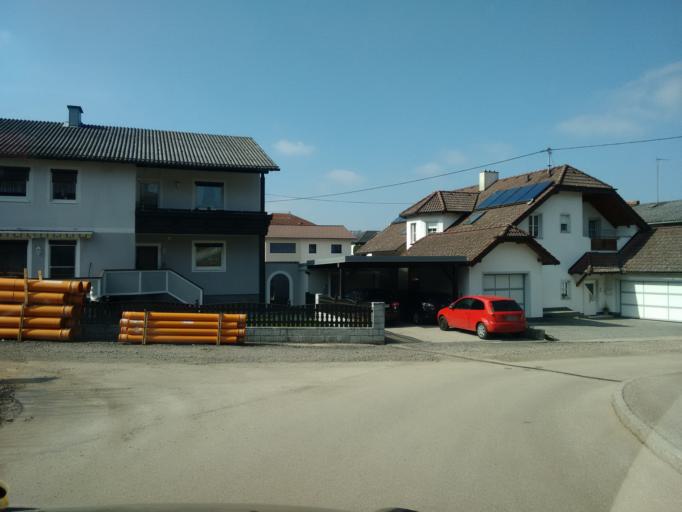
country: AT
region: Upper Austria
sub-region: Wels-Land
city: Buchkirchen
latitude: 48.2099
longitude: 13.9717
